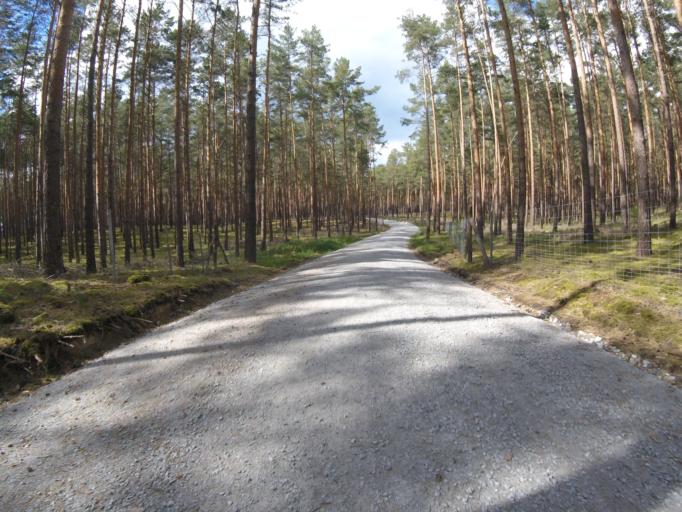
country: DE
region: Brandenburg
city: Schwerin
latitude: 52.1904
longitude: 13.5962
